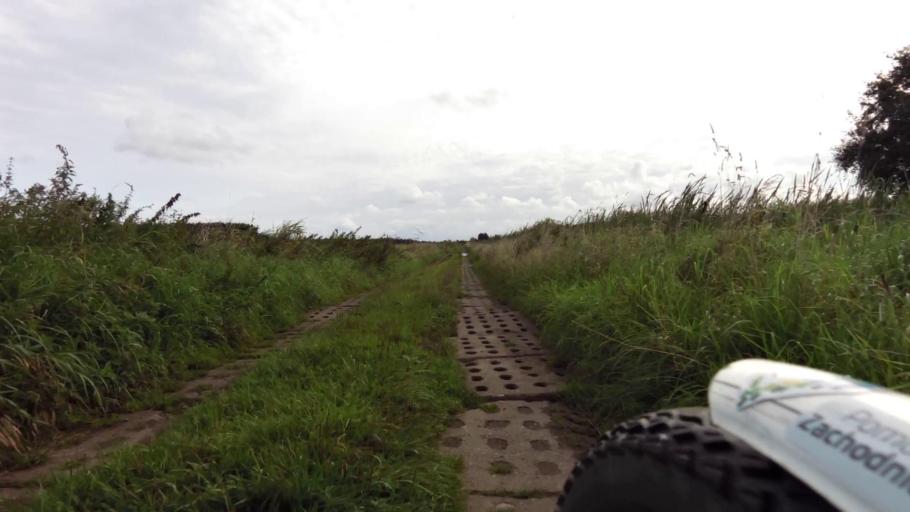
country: PL
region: West Pomeranian Voivodeship
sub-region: Powiat kolobrzeski
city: Grzybowo
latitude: 54.1383
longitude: 15.4393
